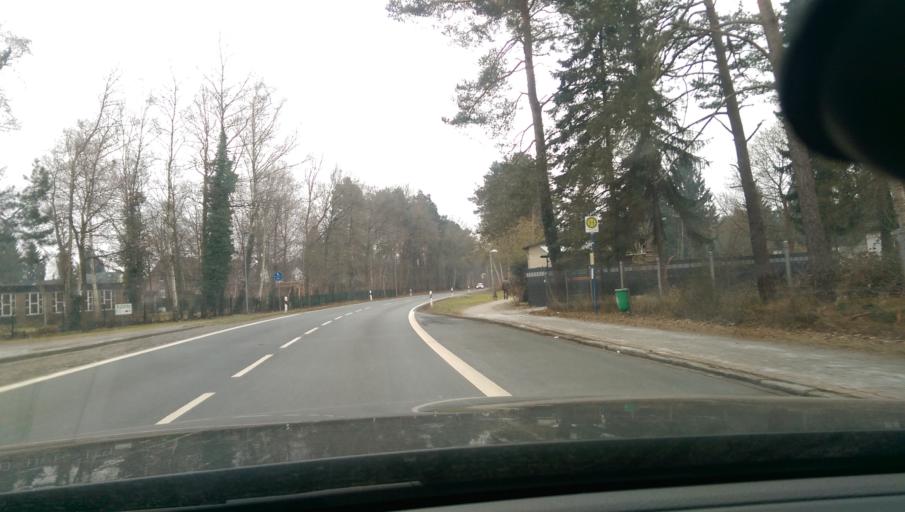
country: DE
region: Lower Saxony
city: Winsen
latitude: 52.6428
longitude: 9.9331
